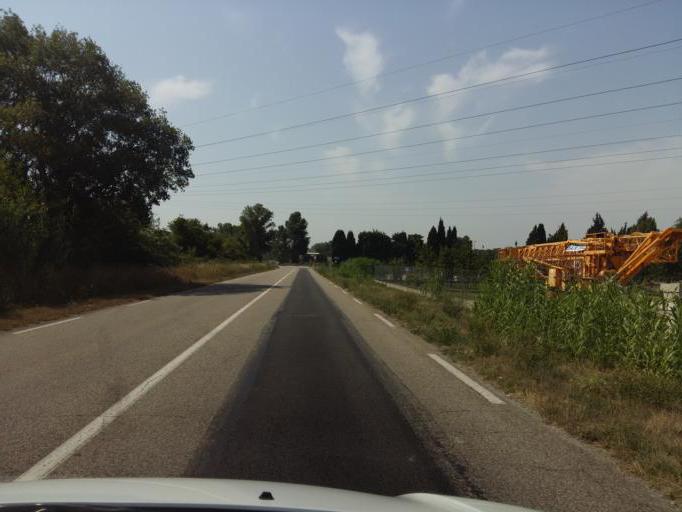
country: FR
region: Provence-Alpes-Cote d'Azur
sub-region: Departement du Vaucluse
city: Bollene
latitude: 44.3151
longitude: 4.7349
